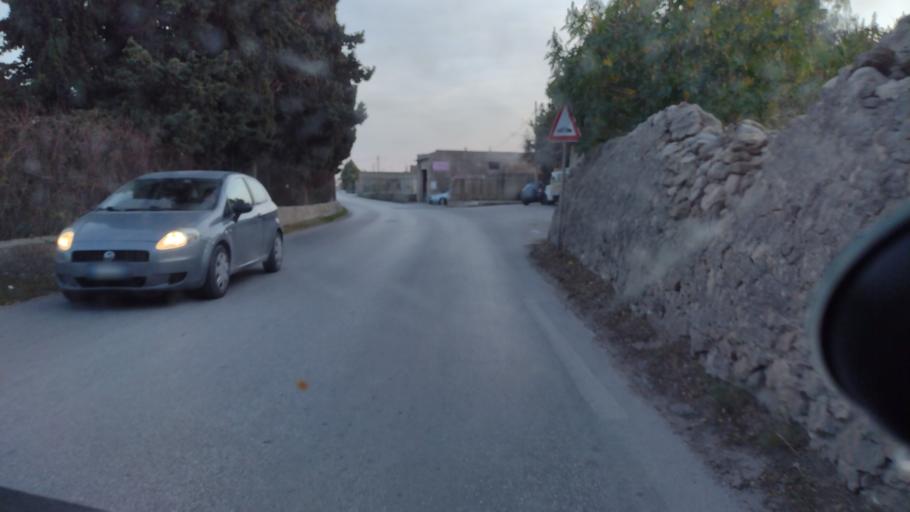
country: IT
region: Sicily
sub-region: Provincia di Siracusa
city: Avola
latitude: 36.8995
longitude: 15.1346
